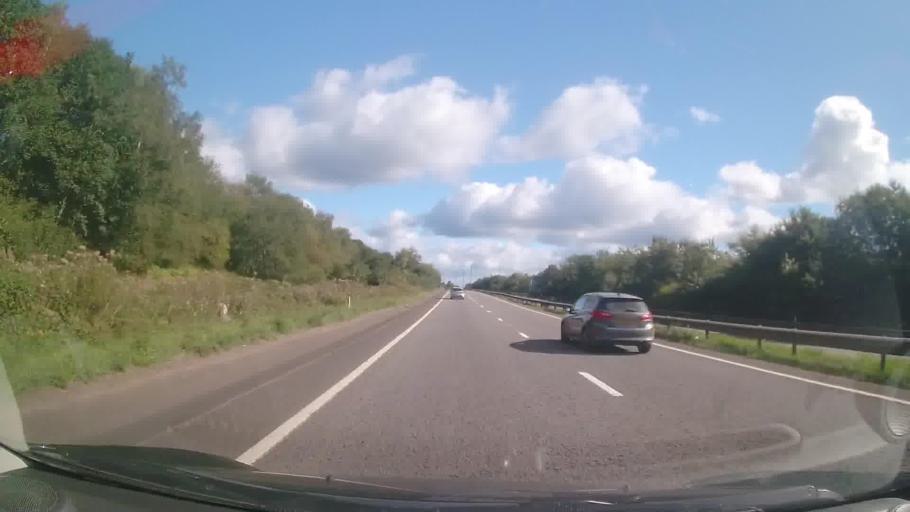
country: GB
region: Wales
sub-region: Neath Port Talbot
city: Neath
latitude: 51.6719
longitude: -3.7926
